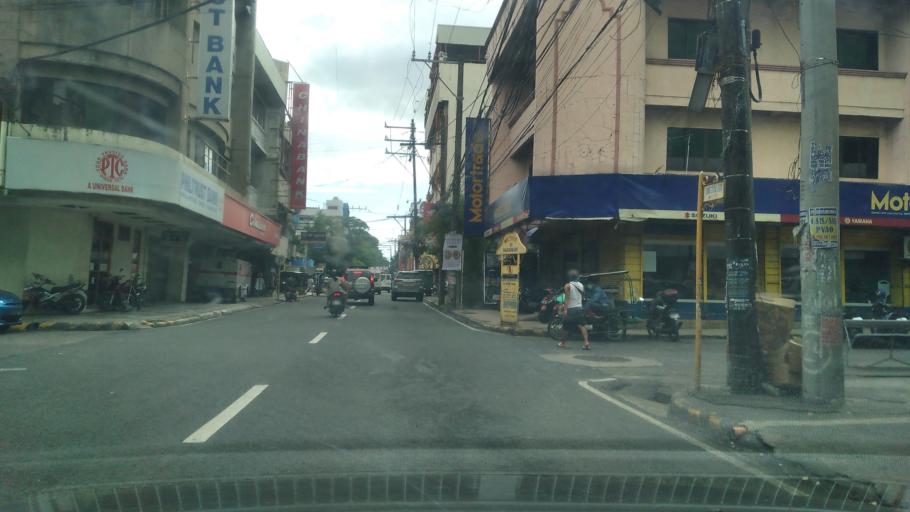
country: PH
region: Calabarzon
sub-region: Province of Quezon
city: Lucena
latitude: 13.9320
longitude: 121.6126
